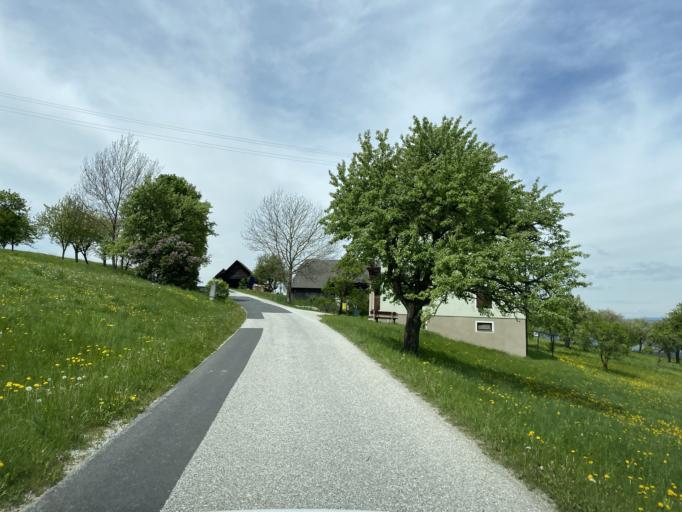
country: AT
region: Styria
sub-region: Politischer Bezirk Weiz
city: Gschaid bei Birkfeld
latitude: 47.3604
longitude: 15.7291
